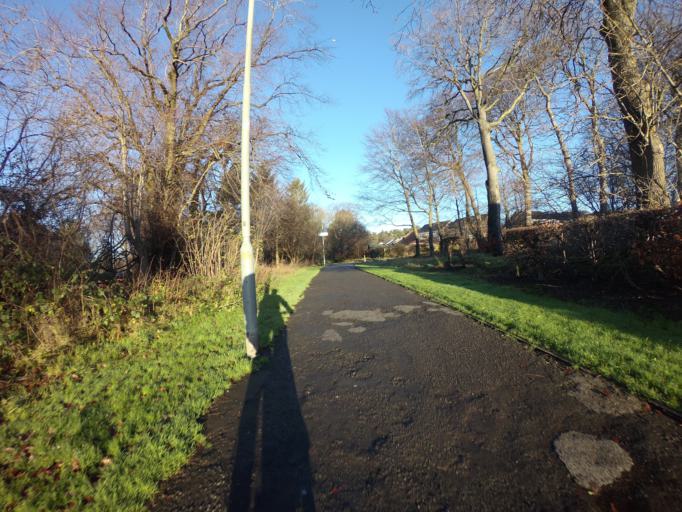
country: GB
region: Scotland
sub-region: West Lothian
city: Livingston
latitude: 55.8969
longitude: -3.5267
